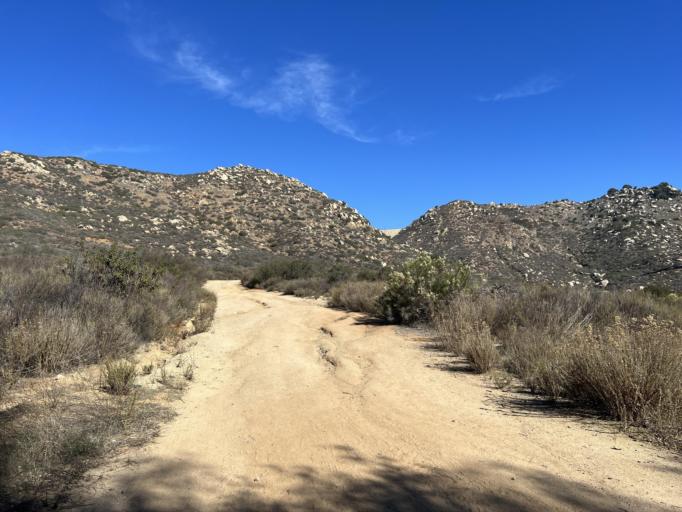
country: US
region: California
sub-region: San Diego County
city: Poway
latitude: 33.0168
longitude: -117.0059
